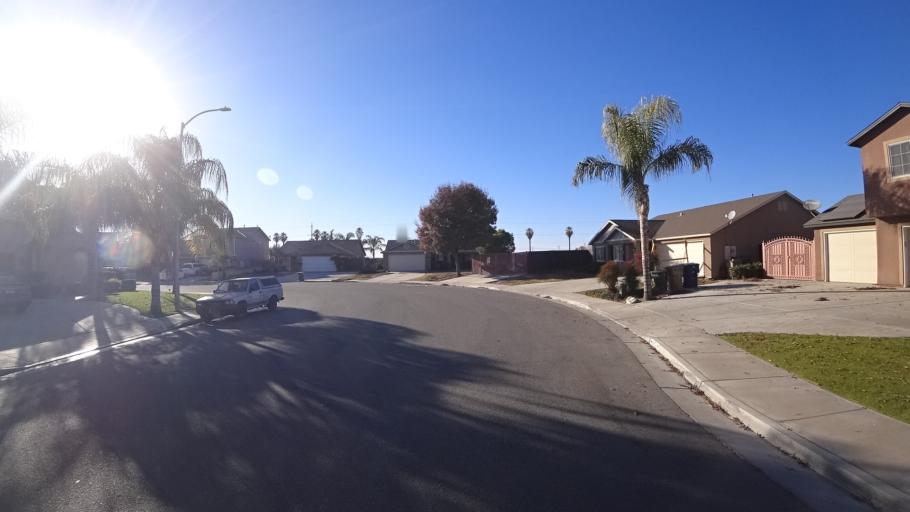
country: US
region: California
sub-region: Kern County
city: Greenfield
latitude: 35.2800
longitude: -119.0010
